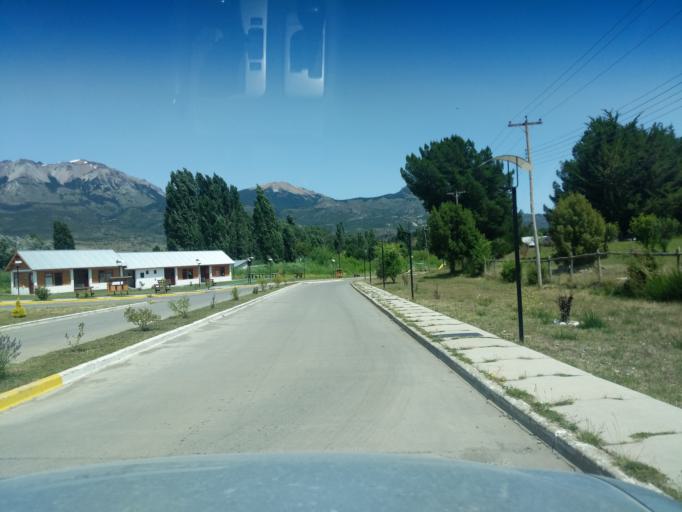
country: CL
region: Los Lagos
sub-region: Provincia de Palena
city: Palena
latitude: -43.5361
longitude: -71.4686
